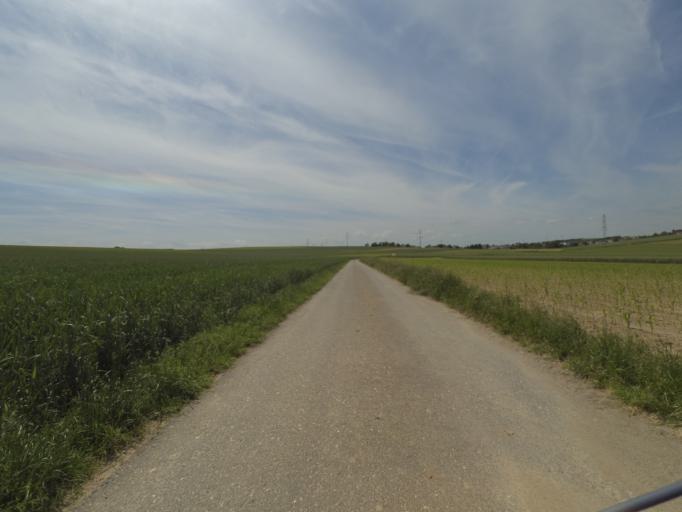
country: DE
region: Rheinland-Pfalz
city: Pillig
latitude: 50.2378
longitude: 7.3259
